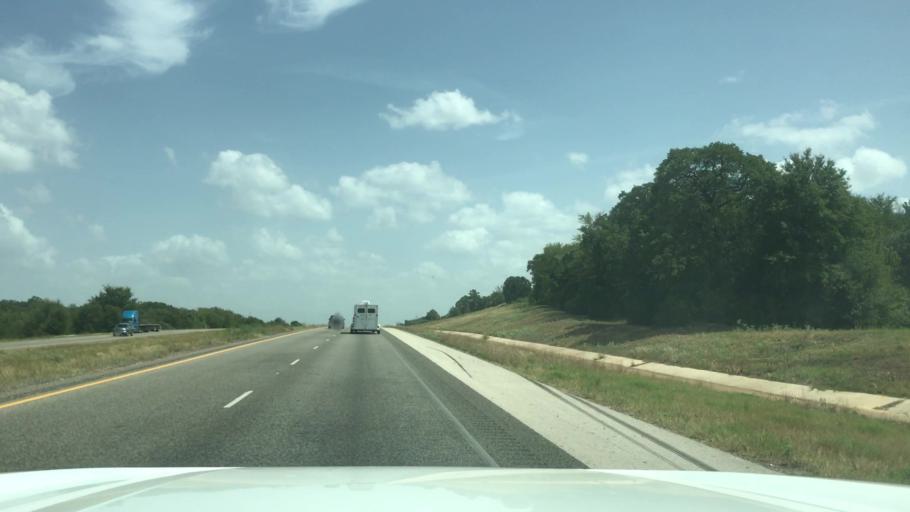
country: US
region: Texas
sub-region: Robertson County
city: Calvert
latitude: 30.9317
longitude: -96.6346
